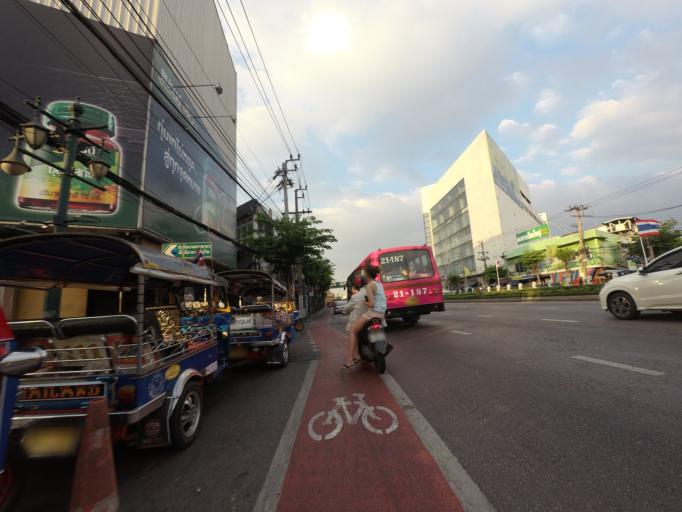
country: TH
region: Bangkok
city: Thon Buri
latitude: 13.7247
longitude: 100.4924
